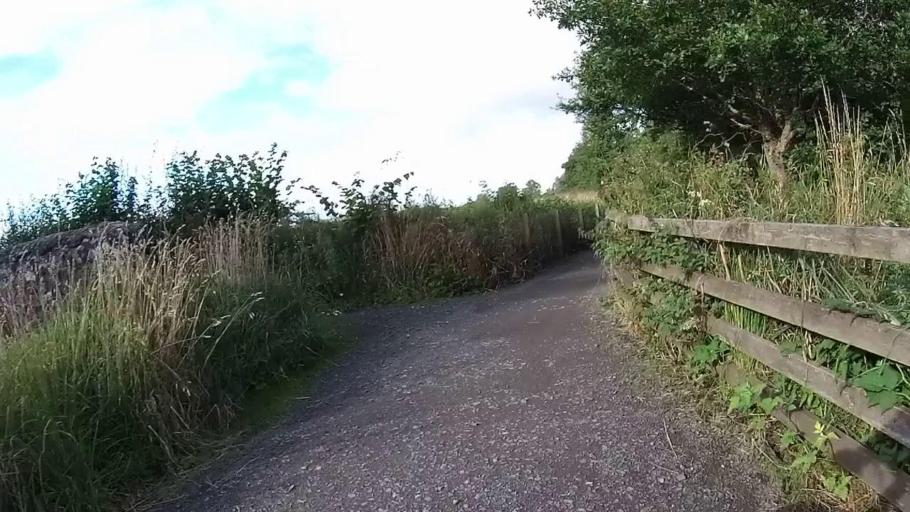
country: GB
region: Scotland
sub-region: Perth and Kinross
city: Milnathort
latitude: 56.2151
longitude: -3.4049
